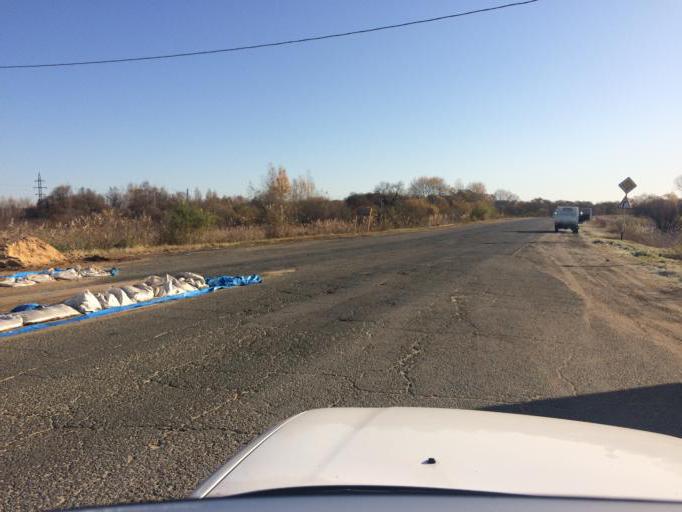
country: RU
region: Primorskiy
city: Dal'nerechensk
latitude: 45.9177
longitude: 133.7730
